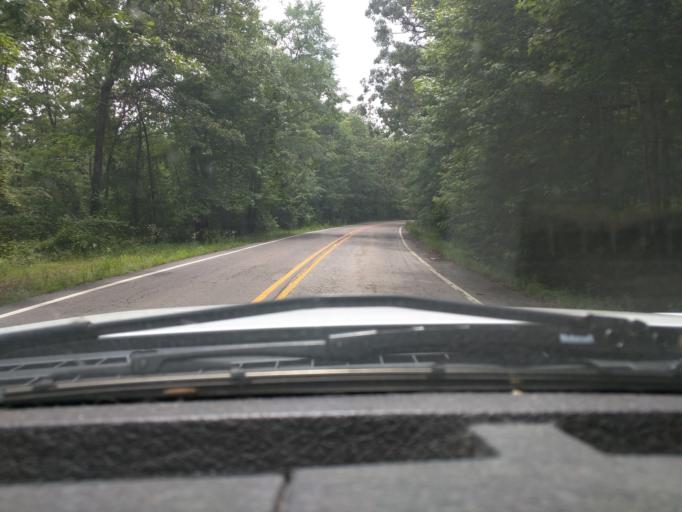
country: US
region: Arkansas
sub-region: Franklin County
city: Ozark
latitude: 35.6958
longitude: -93.8019
